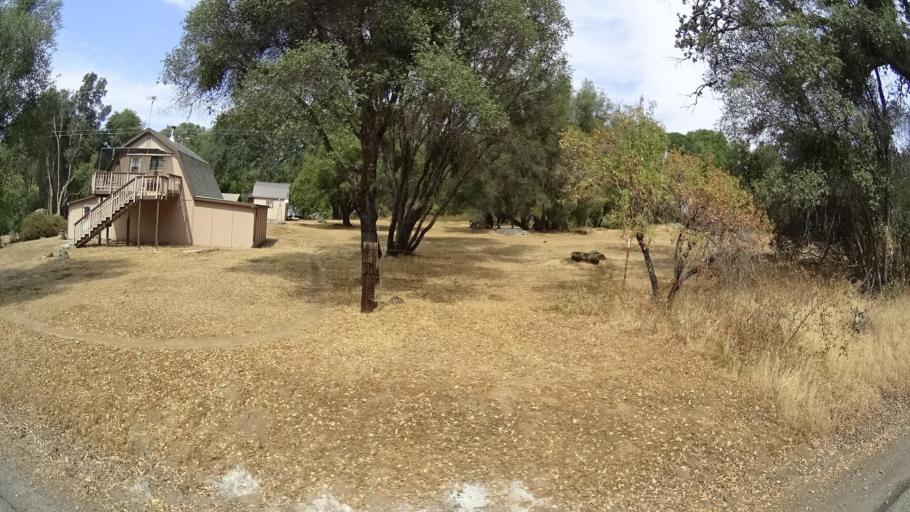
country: US
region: California
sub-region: Mariposa County
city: Midpines
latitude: 37.4864
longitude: -119.9051
